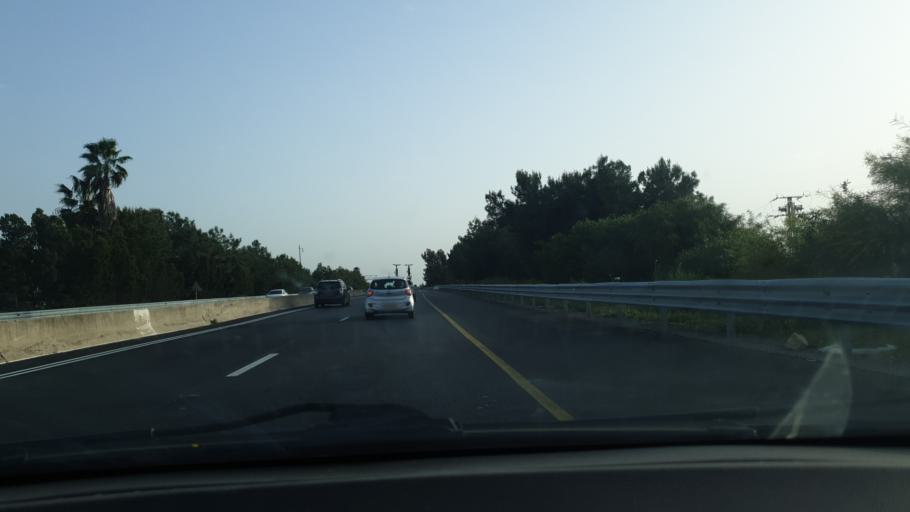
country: IL
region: Central District
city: Even Yehuda
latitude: 32.2369
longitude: 34.8857
